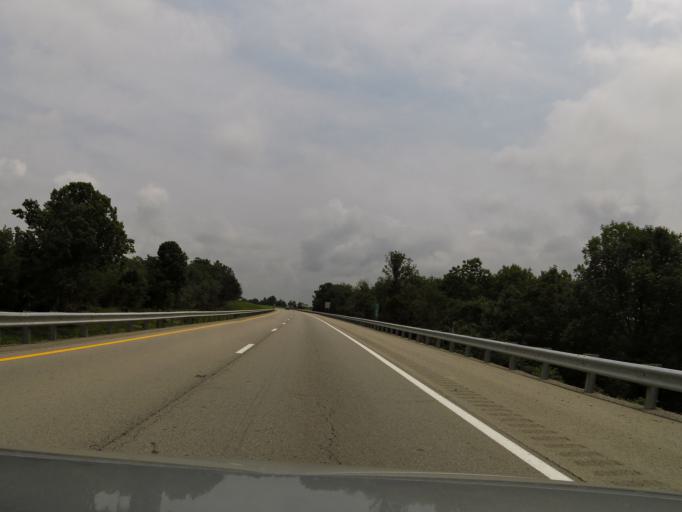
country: US
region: Kentucky
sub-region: Grayson County
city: Leitchfield
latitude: 37.4667
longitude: -86.2740
